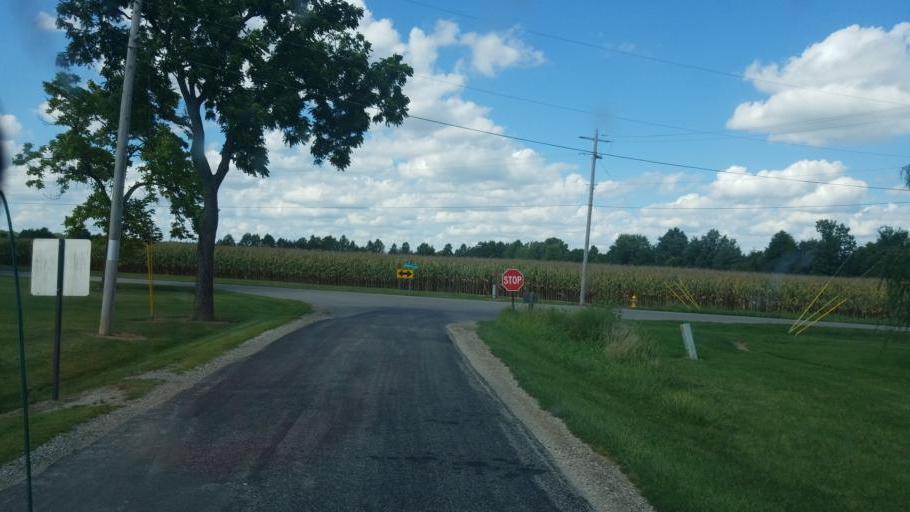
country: US
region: Ohio
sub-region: Union County
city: Richwood
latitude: 40.3155
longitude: -83.2221
